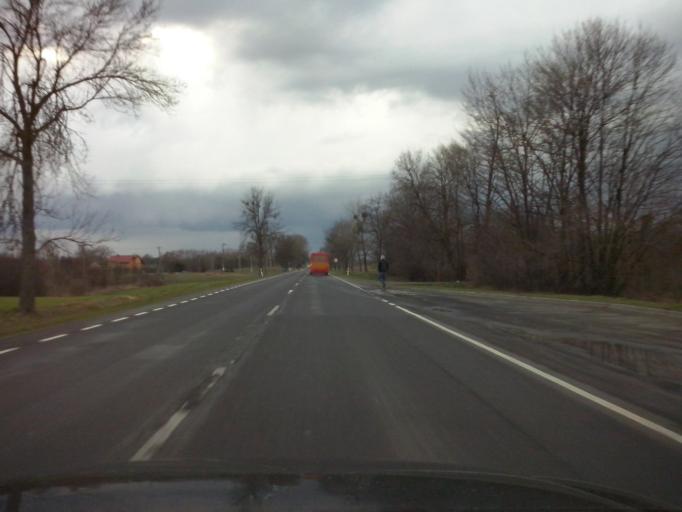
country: PL
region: Lublin Voivodeship
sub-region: Powiat chelmski
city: Rejowiec Fabryczny
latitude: 51.1722
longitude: 23.2936
